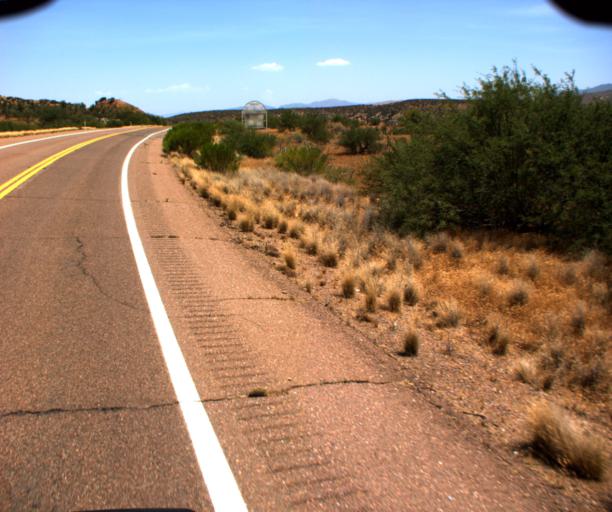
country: US
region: Arizona
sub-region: Gila County
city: Tonto Basin
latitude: 33.8085
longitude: -111.2835
